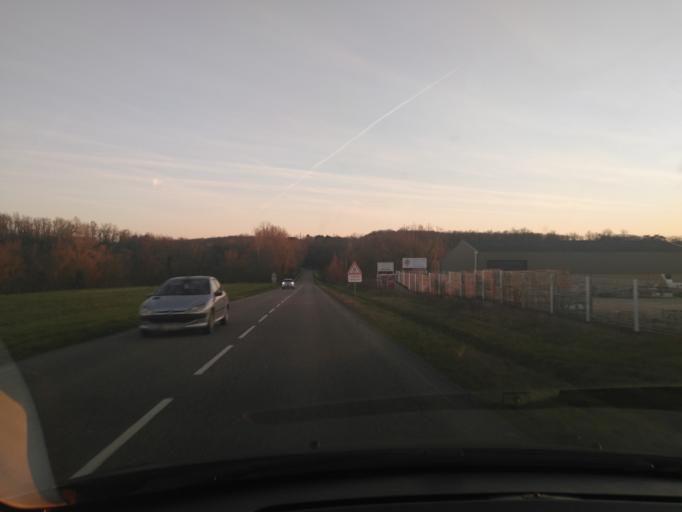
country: FR
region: Aquitaine
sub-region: Departement du Lot-et-Garonne
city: Villeneuve-sur-Lot
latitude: 44.4627
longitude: 0.7267
